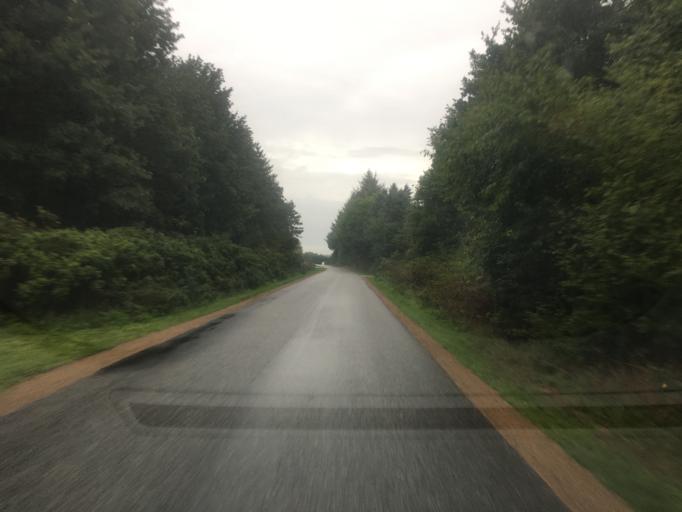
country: DK
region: South Denmark
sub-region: Tonder Kommune
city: Logumkloster
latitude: 55.0191
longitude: 9.0351
